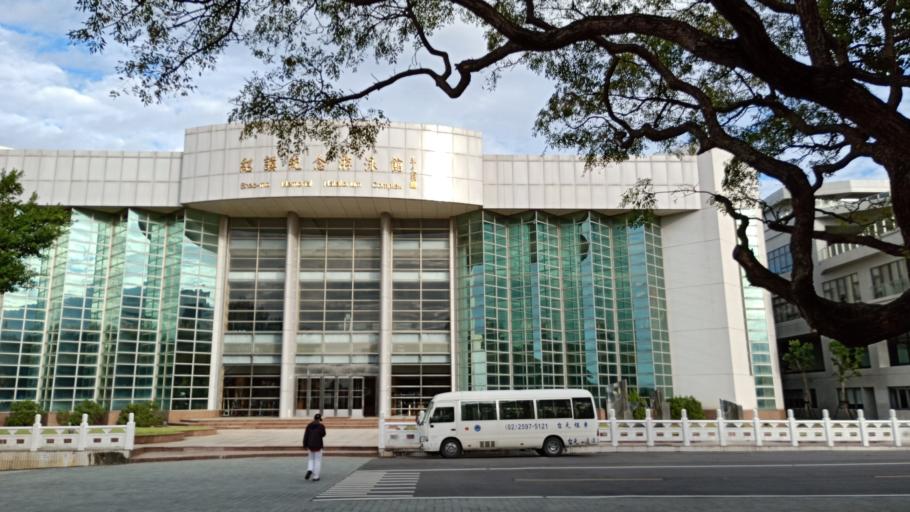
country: TW
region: Taipei
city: Taipei
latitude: 25.1740
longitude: 121.4476
